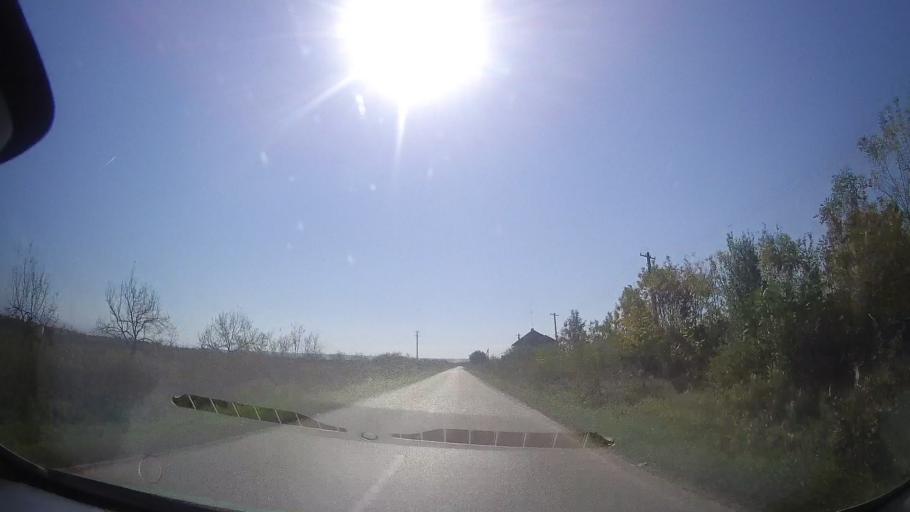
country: RO
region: Timis
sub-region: Comuna Bethausen
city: Bethausen
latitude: 45.8270
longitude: 21.9596
